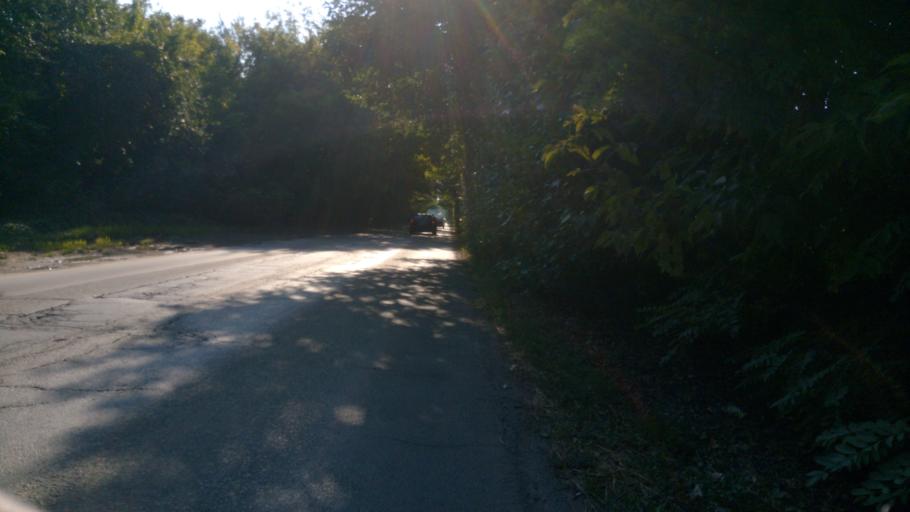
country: HU
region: Pest
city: Budaors
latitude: 47.4475
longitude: 18.9819
